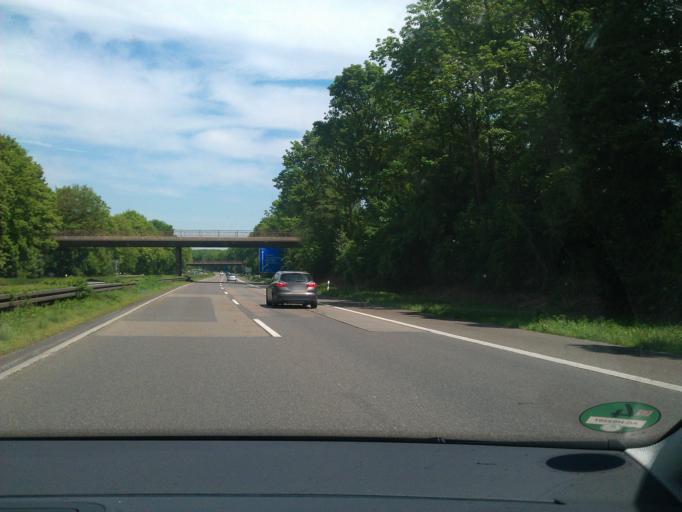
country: DE
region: North Rhine-Westphalia
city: Siersdorf
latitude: 50.8596
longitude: 6.2090
